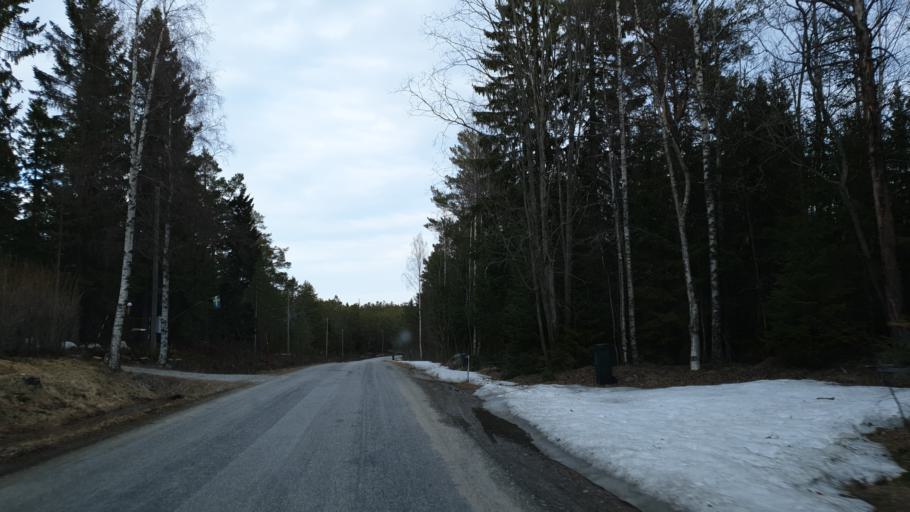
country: SE
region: Vaesternorrland
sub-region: Sundsvalls Kommun
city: Njurundabommen
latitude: 61.9642
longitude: 17.3715
